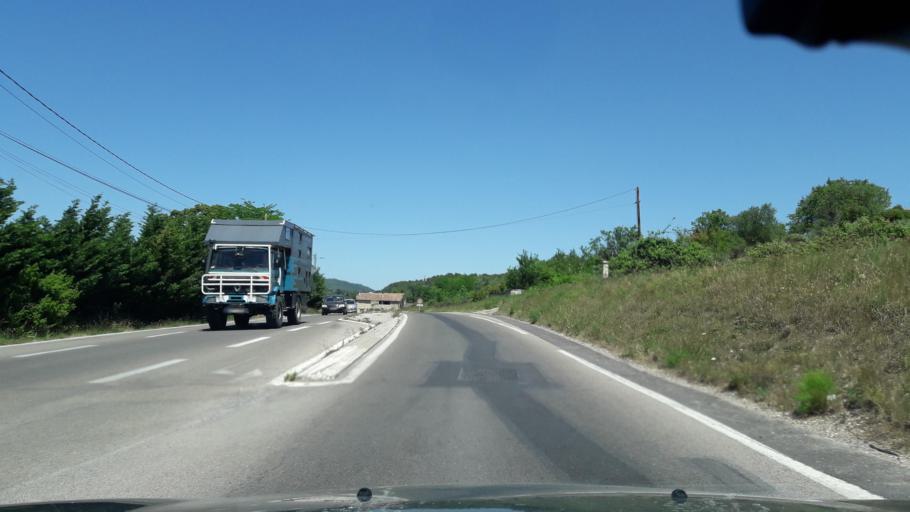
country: FR
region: Languedoc-Roussillon
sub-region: Departement du Gard
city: Rousson
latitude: 44.1846
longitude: 4.1273
